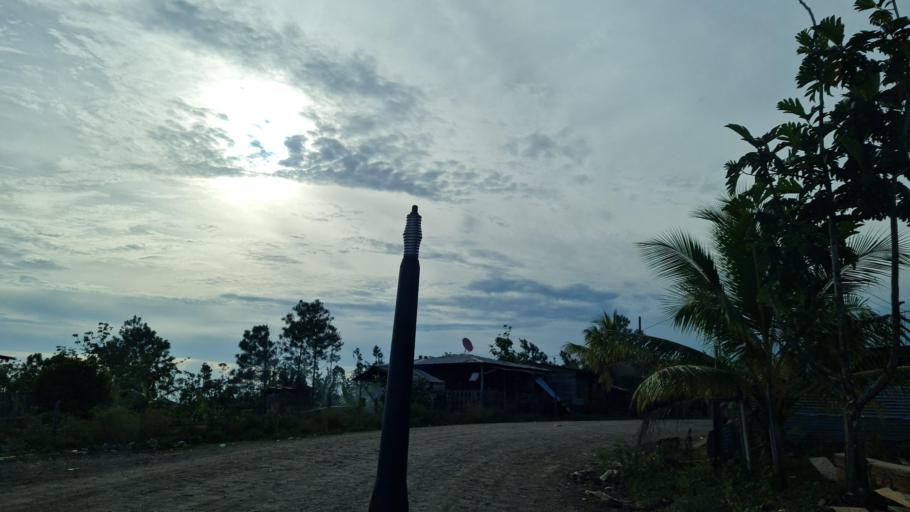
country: NI
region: Atlantico Sur
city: La Cruz de Rio Grande
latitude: 13.5644
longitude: -84.3137
